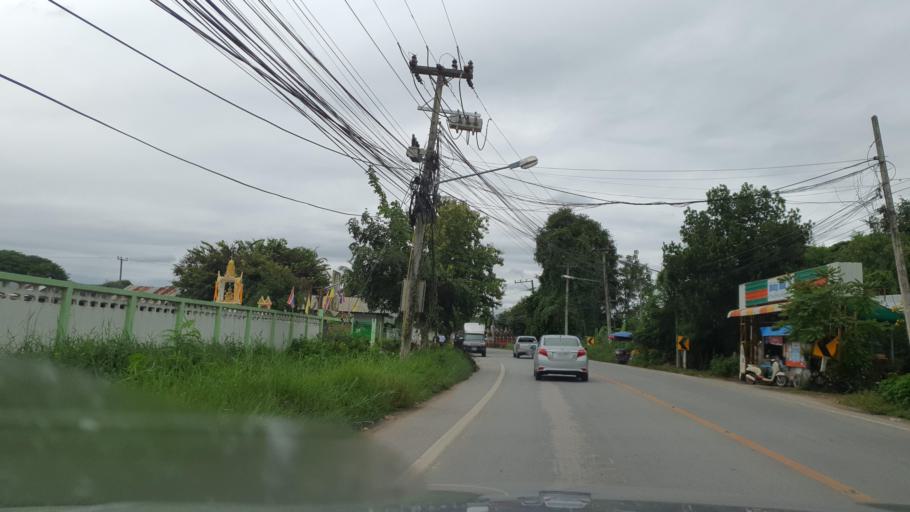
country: TH
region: Chiang Mai
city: San Pa Tong
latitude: 18.6248
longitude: 98.9306
